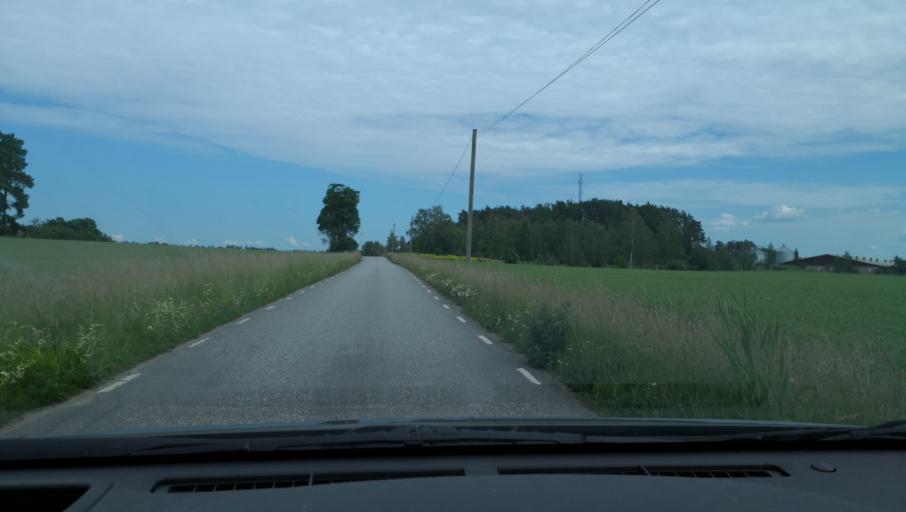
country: SE
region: Uppsala
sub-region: Enkopings Kommun
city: Orsundsbro
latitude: 59.6952
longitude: 17.3981
